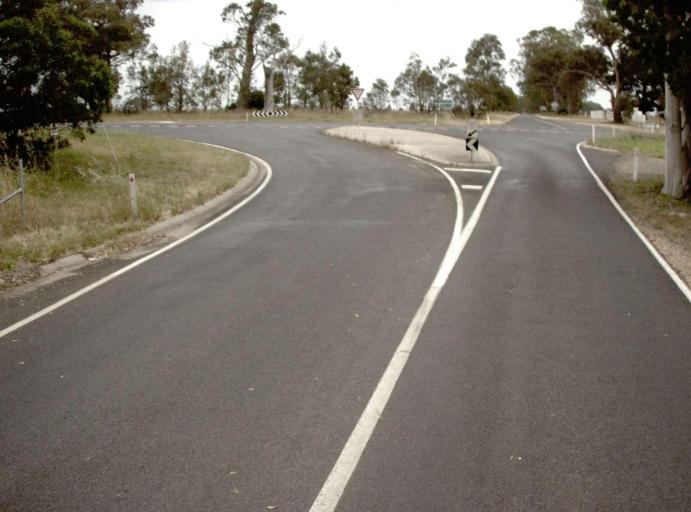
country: AU
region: Victoria
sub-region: East Gippsland
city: Bairnsdale
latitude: -37.8803
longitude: 147.4228
